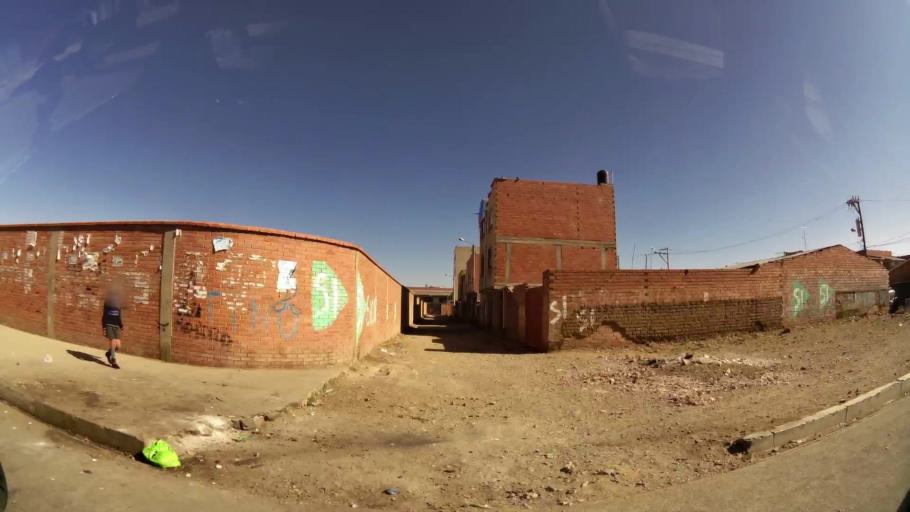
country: BO
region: La Paz
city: La Paz
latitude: -16.5241
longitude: -68.2072
